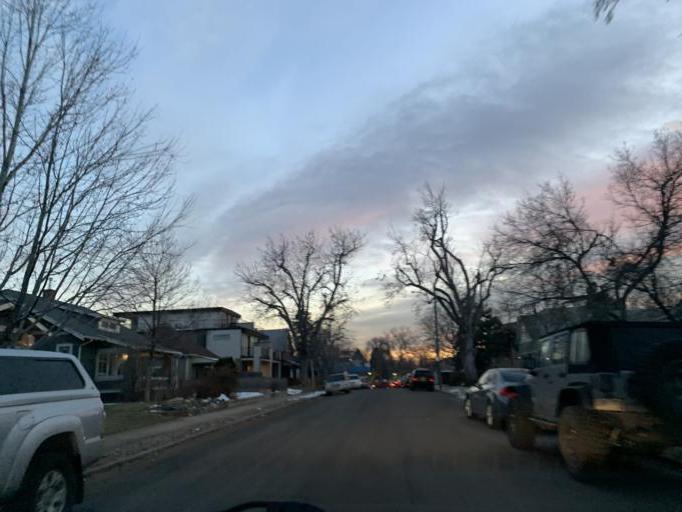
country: US
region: Colorado
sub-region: Adams County
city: Berkley
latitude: 39.7779
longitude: -105.0428
